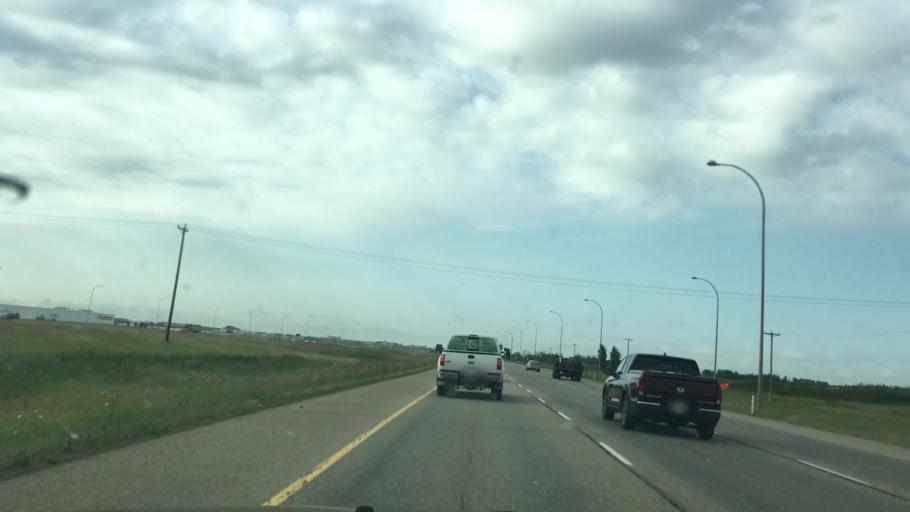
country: CA
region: Alberta
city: Leduc
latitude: 53.3355
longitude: -113.5503
